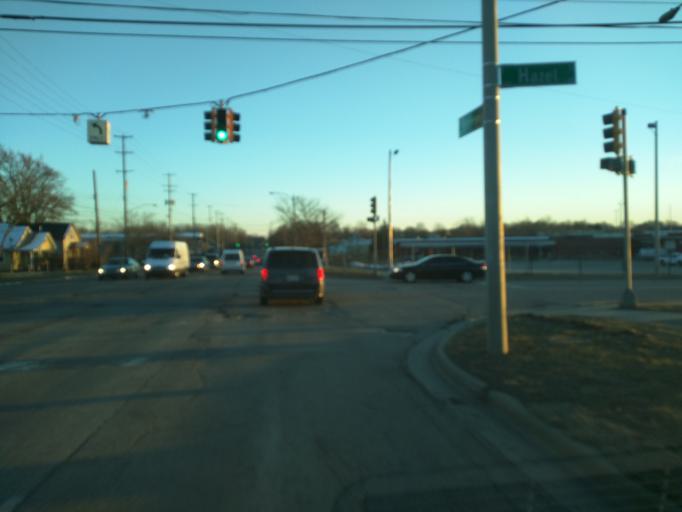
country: US
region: Michigan
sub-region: Ingham County
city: Lansing
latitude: 42.7234
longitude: -84.5382
